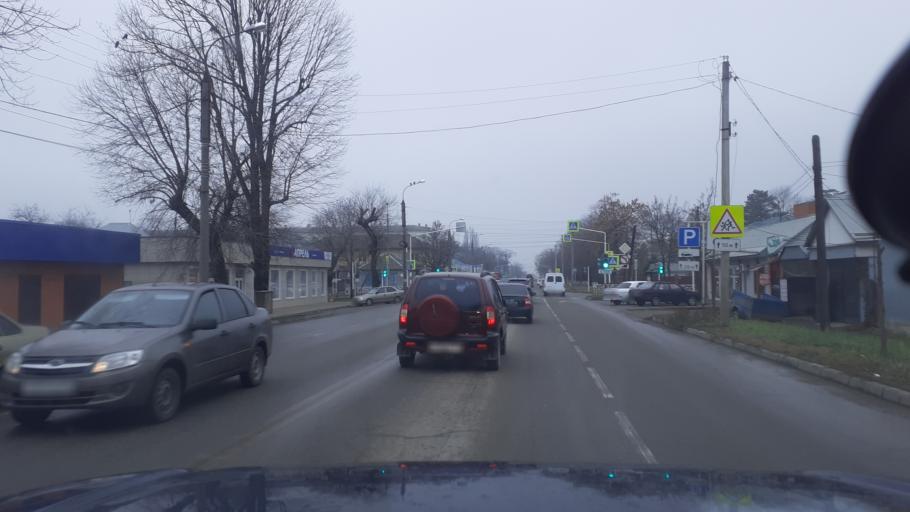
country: RU
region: Adygeya
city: Maykop
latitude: 44.6169
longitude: 40.1125
